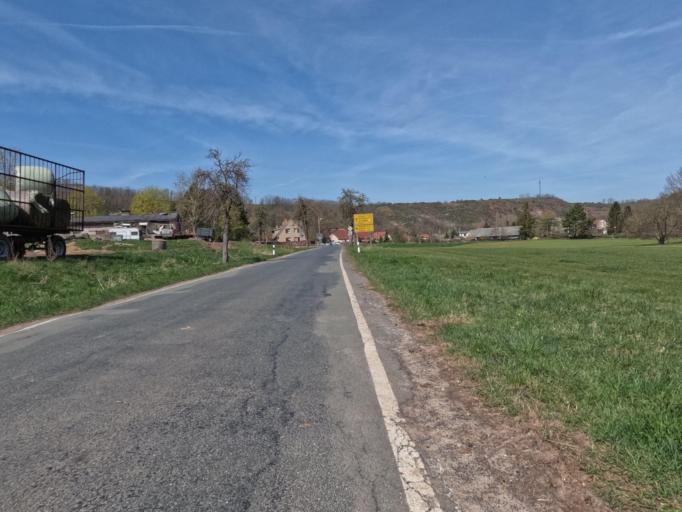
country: DE
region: Saxony-Anhalt
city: Konnern
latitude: 51.6371
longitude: 11.7471
